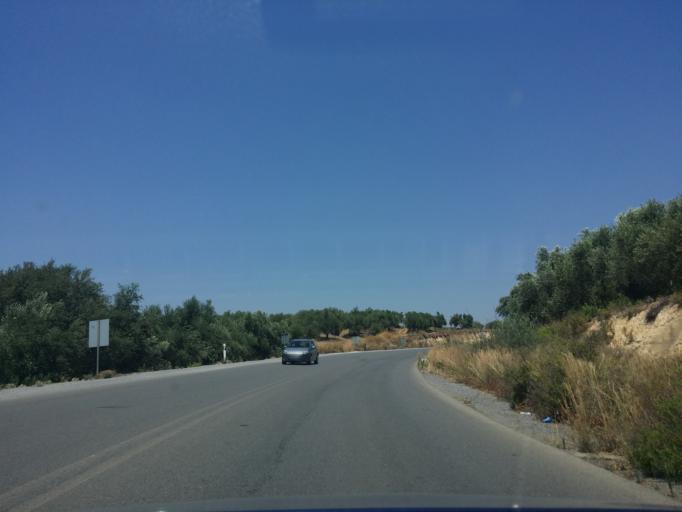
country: GR
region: Peloponnese
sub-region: Nomos Lakonias
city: Vlakhiotis
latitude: 36.8521
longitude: 22.7377
